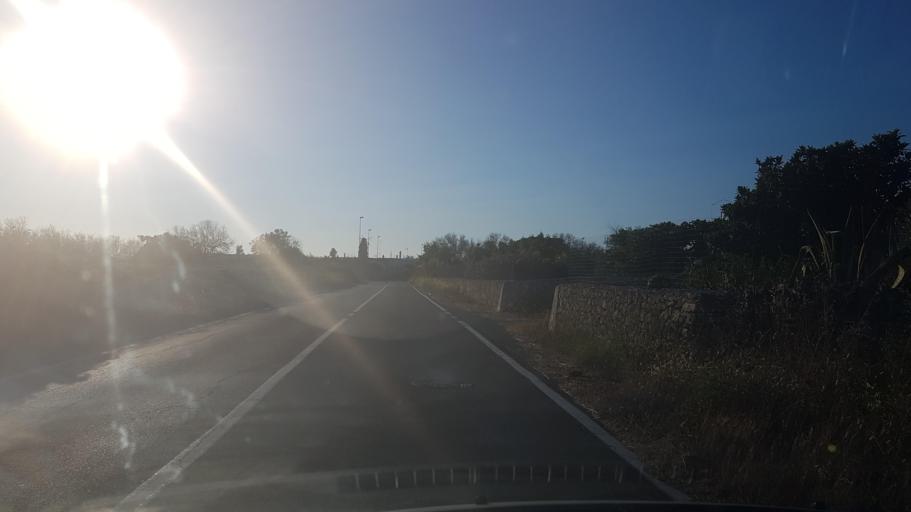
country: IT
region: Apulia
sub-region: Provincia di Lecce
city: Struda
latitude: 40.3313
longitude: 18.2989
